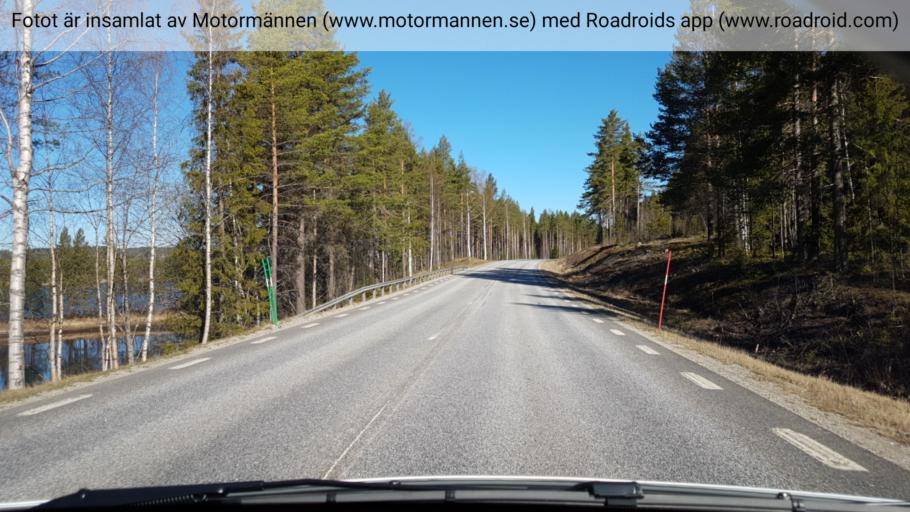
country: SE
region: Vaesterbotten
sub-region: Lycksele Kommun
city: Lycksele
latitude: 64.5483
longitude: 18.7397
